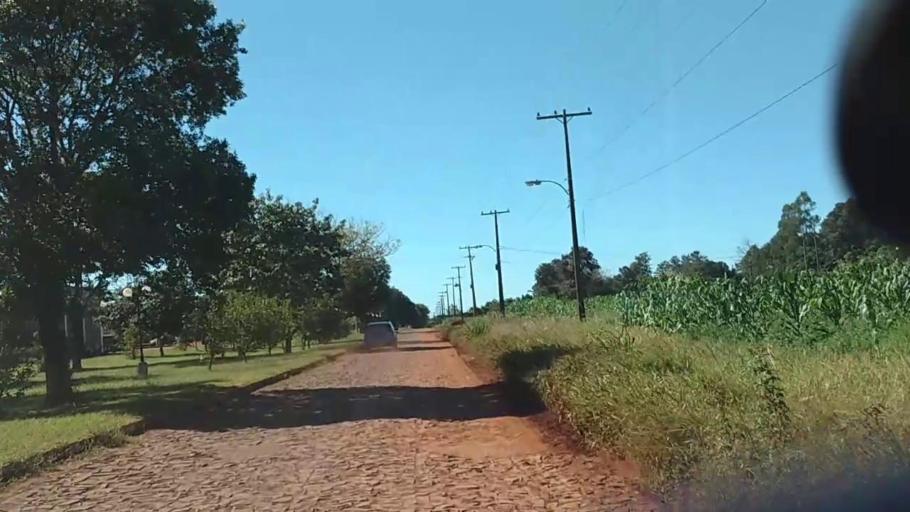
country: PY
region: Alto Parana
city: Naranjal
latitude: -25.9722
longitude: -55.1989
